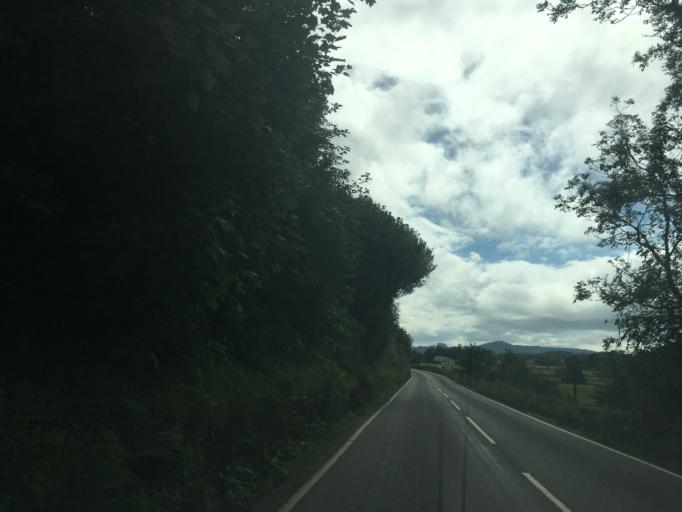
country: GB
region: Scotland
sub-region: Argyll and Bute
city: Lochgilphead
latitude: 56.1313
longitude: -5.4844
